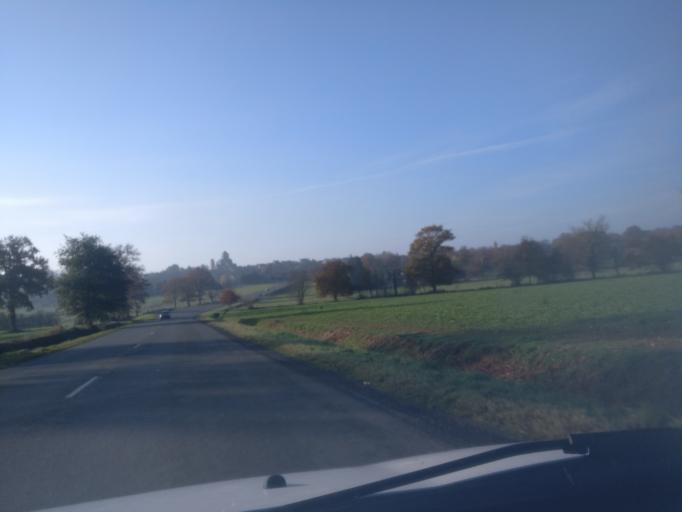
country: FR
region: Brittany
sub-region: Departement d'Ille-et-Vilaine
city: Saint-Aubin-du-Cormier
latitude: 48.2681
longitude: -1.3929
